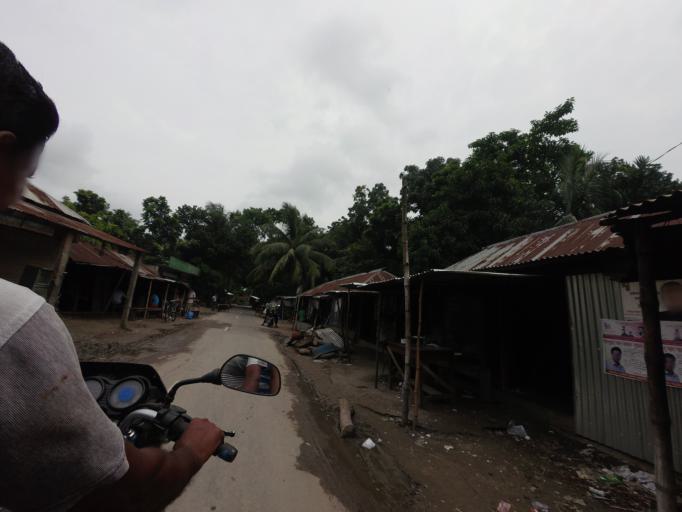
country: BD
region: Khulna
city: Kalia
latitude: 23.1034
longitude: 89.6475
